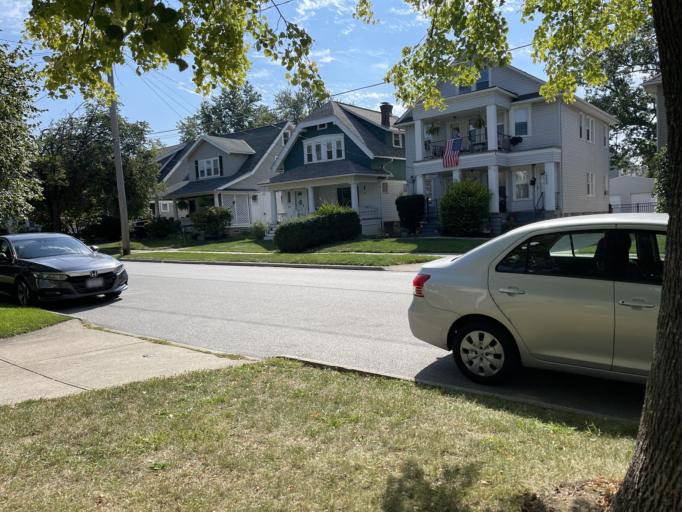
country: US
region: Ohio
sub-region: Cuyahoga County
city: Lakewood
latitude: 41.4907
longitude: -81.8004
